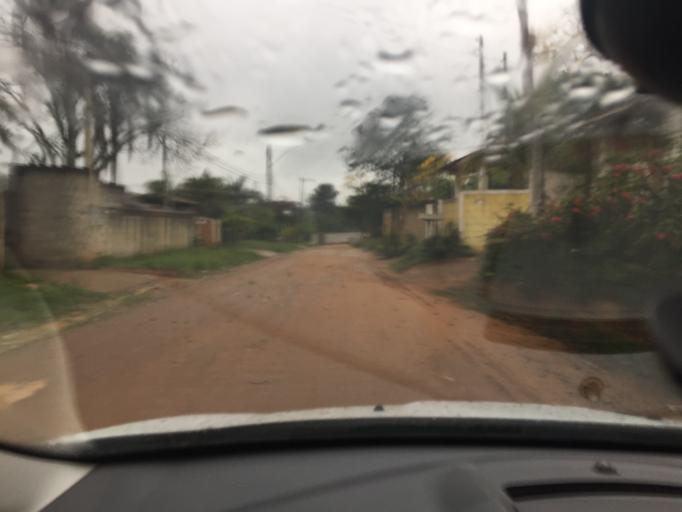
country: BR
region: Sao Paulo
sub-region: Jarinu
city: Jarinu
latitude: -23.1396
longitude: -46.7272
